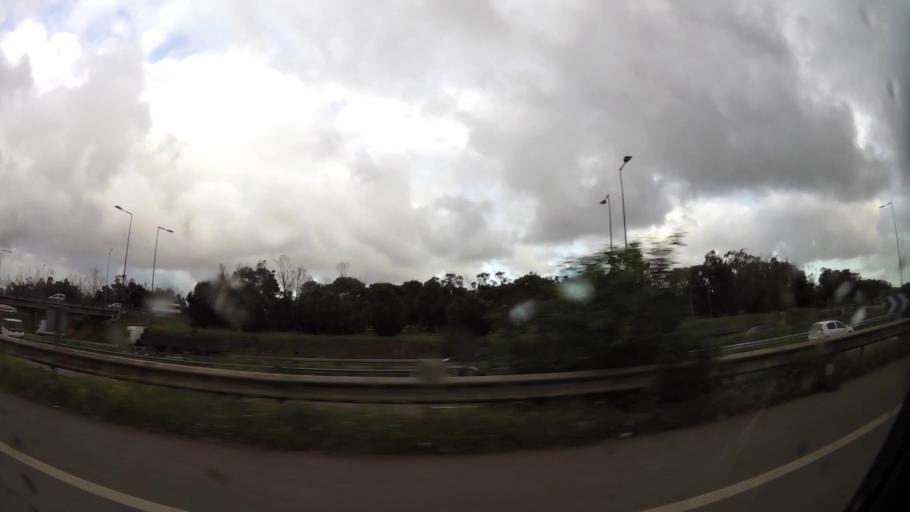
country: MA
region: Grand Casablanca
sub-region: Mohammedia
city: Mohammedia
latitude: 33.6619
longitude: -7.4050
